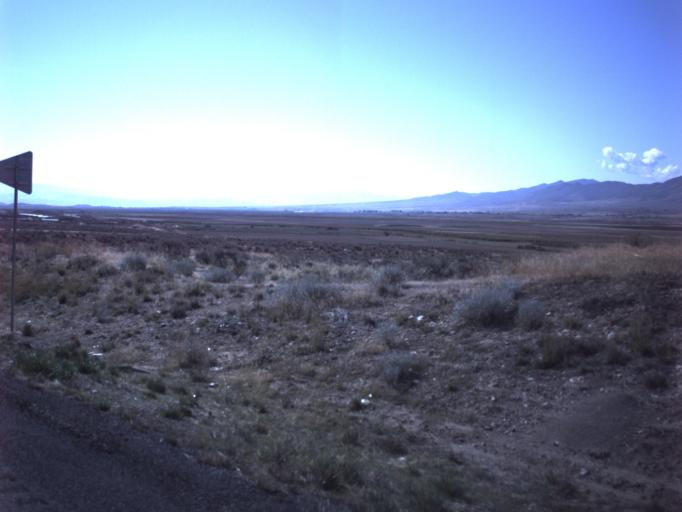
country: US
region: Utah
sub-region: Sanpete County
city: Gunnison
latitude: 39.2769
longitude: -111.8767
